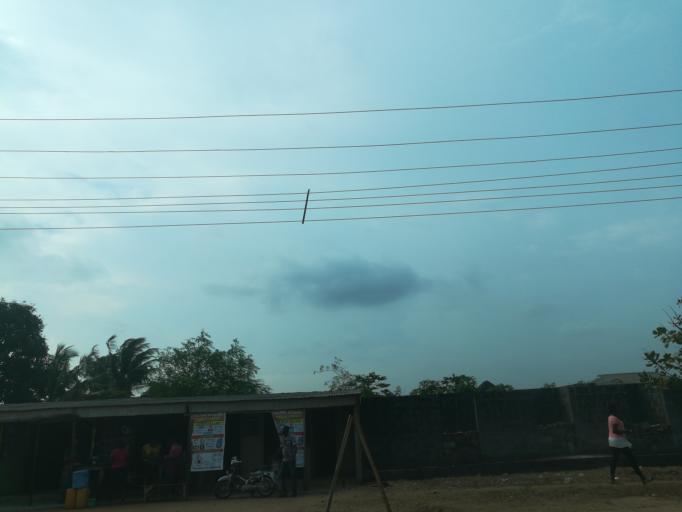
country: NG
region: Lagos
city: Ikorodu
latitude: 6.6133
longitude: 3.6000
